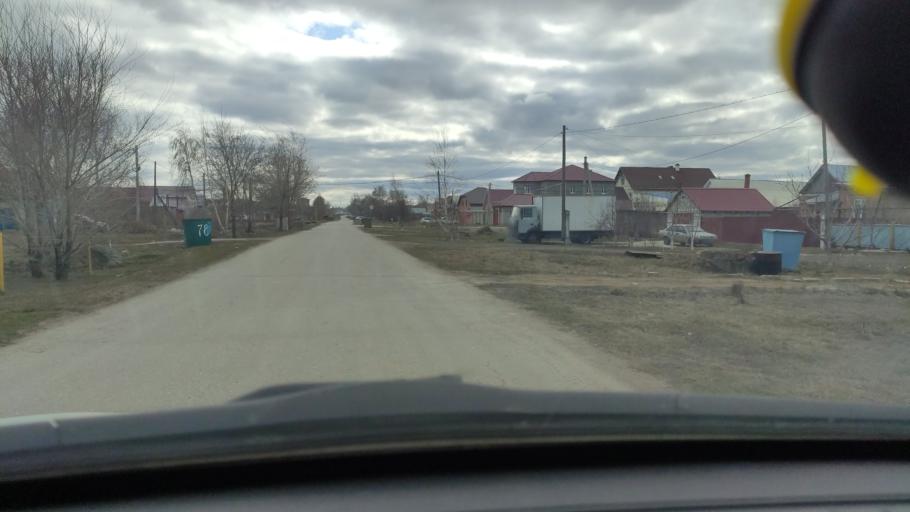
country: RU
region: Samara
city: Tol'yatti
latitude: 53.5641
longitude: 49.4001
